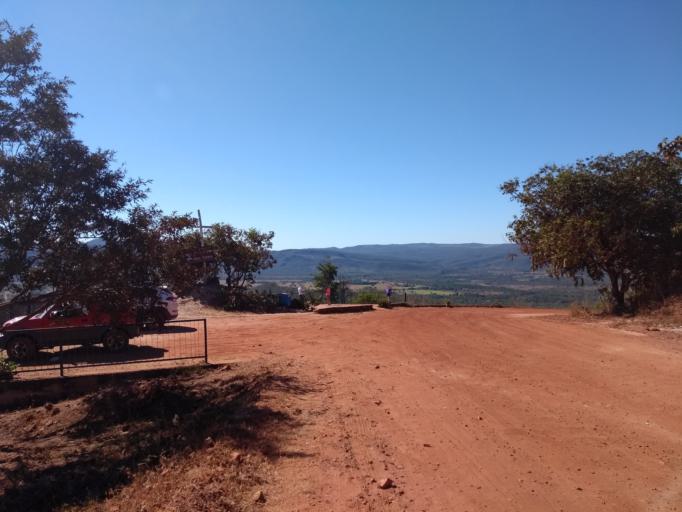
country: BR
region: Goias
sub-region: Cavalcante
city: Cavalcante
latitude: -13.6920
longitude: -47.4661
